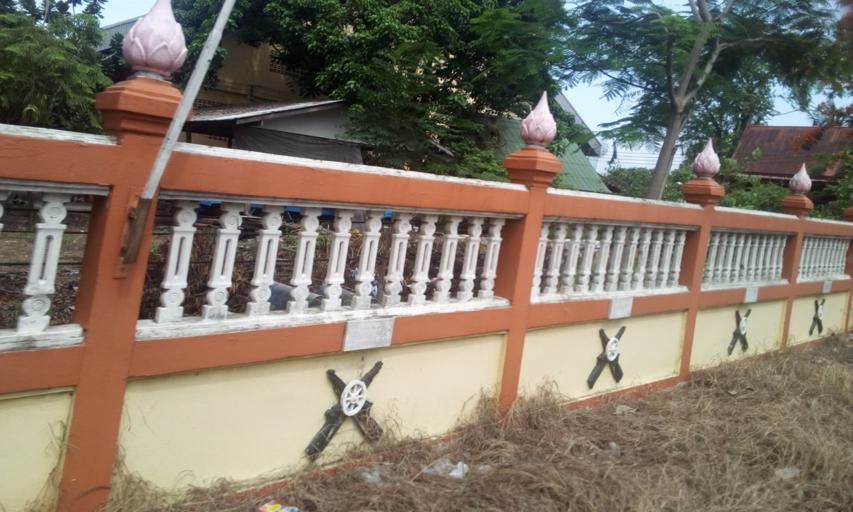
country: TH
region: Pathum Thani
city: Ban Lam Luk Ka
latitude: 14.0015
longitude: 100.8424
